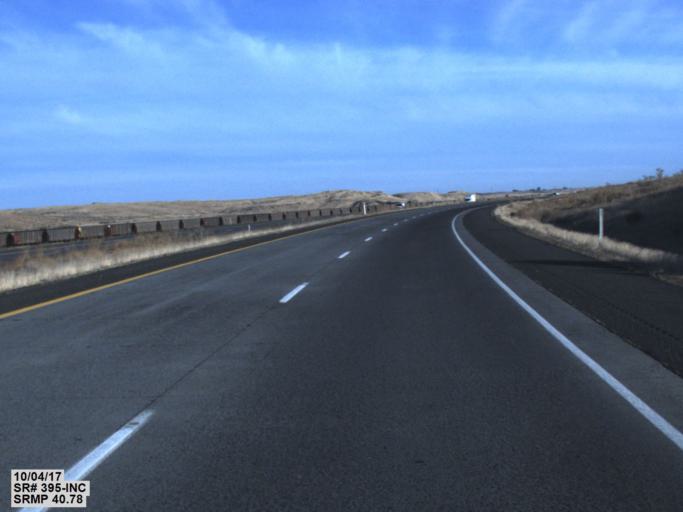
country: US
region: Washington
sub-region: Franklin County
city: Basin City
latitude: 46.4969
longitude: -119.0150
